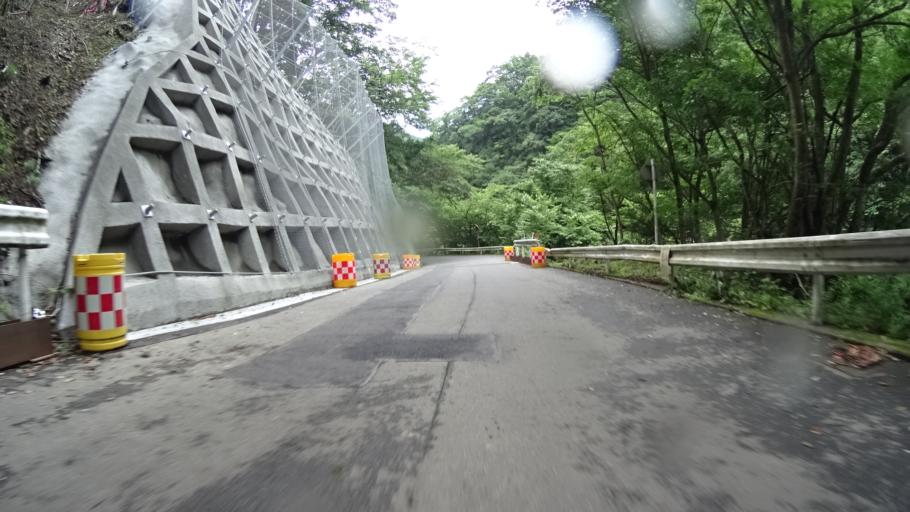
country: JP
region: Kanagawa
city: Hadano
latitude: 35.4845
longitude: 139.2057
